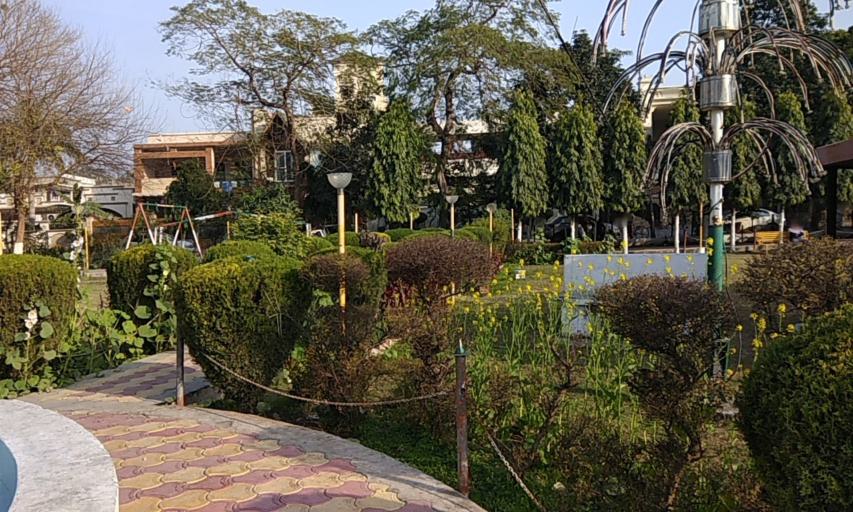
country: IN
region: Punjab
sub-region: Amritsar
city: Amritsar
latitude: 31.6413
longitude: 74.8646
